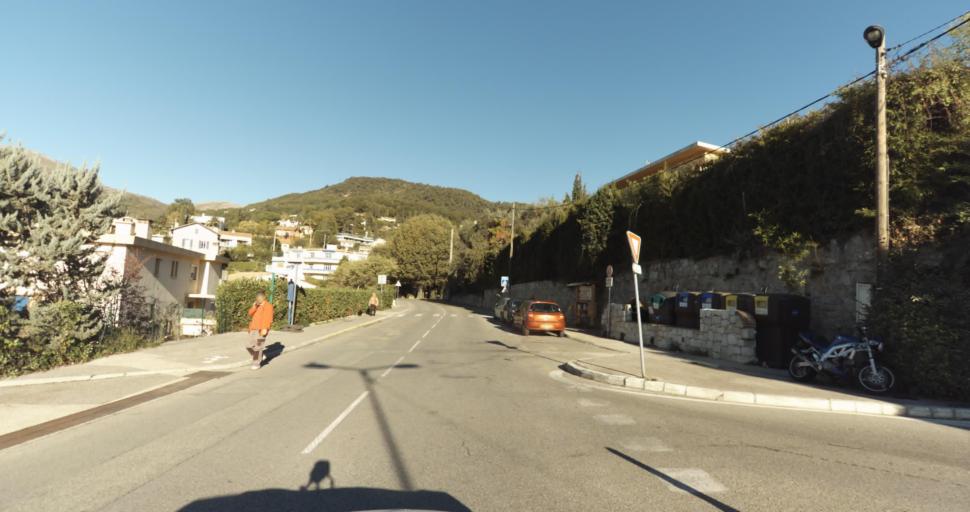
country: FR
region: Provence-Alpes-Cote d'Azur
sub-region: Departement des Alpes-Maritimes
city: Vence
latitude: 43.7247
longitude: 7.1036
